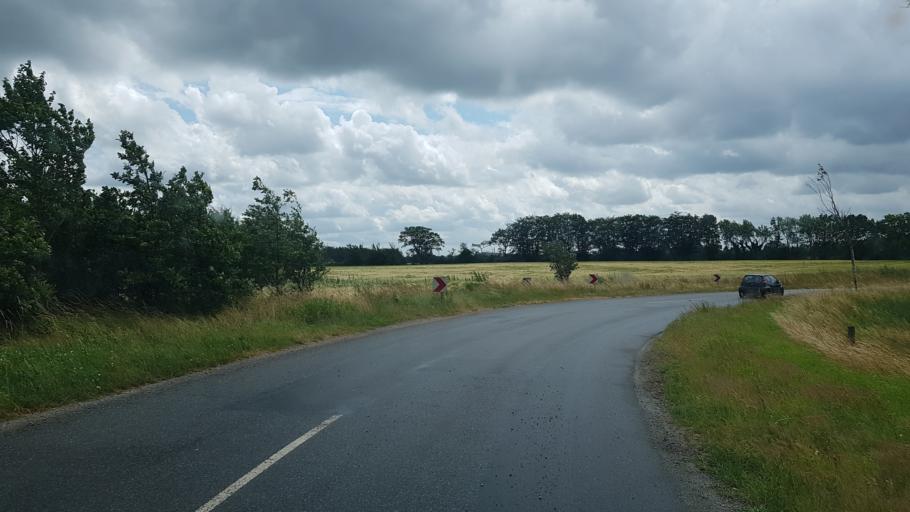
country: DK
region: South Denmark
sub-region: Kolding Kommune
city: Lunderskov
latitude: 55.4686
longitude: 9.2922
